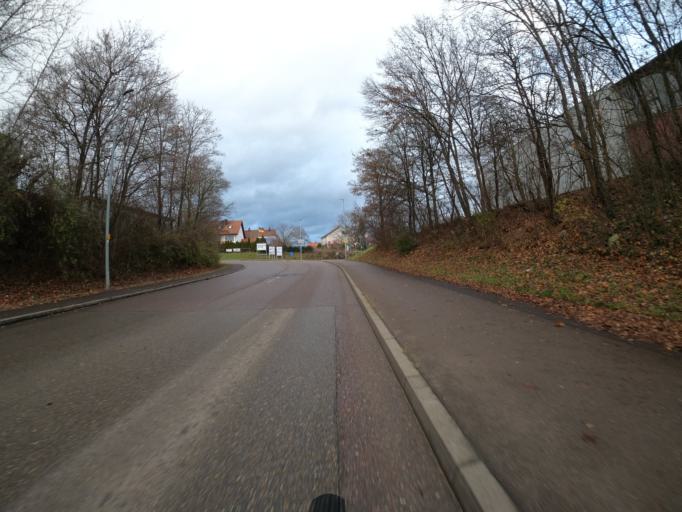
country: DE
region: Baden-Wuerttemberg
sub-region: Regierungsbezirk Stuttgart
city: Salach
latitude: 48.6846
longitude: 9.7368
